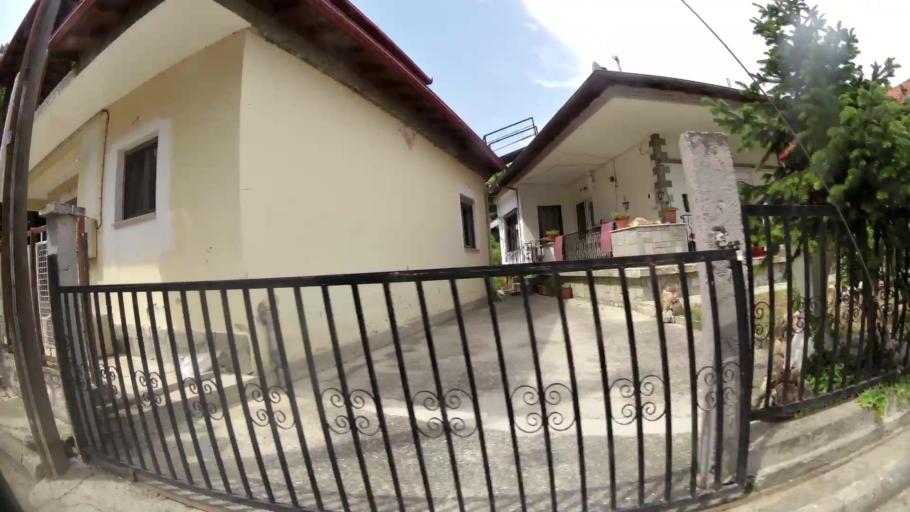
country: GR
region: Central Macedonia
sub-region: Nomos Pierias
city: Korinos
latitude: 40.3128
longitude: 22.5895
